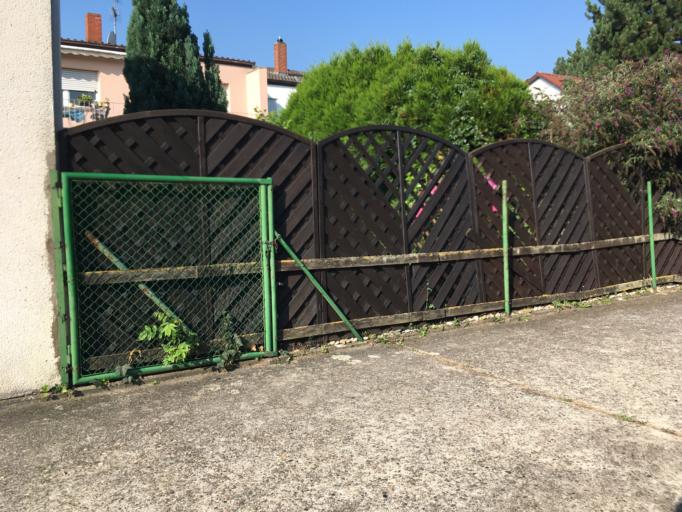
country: DE
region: Rheinland-Pfalz
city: Speyer
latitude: 49.3081
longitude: 8.4244
